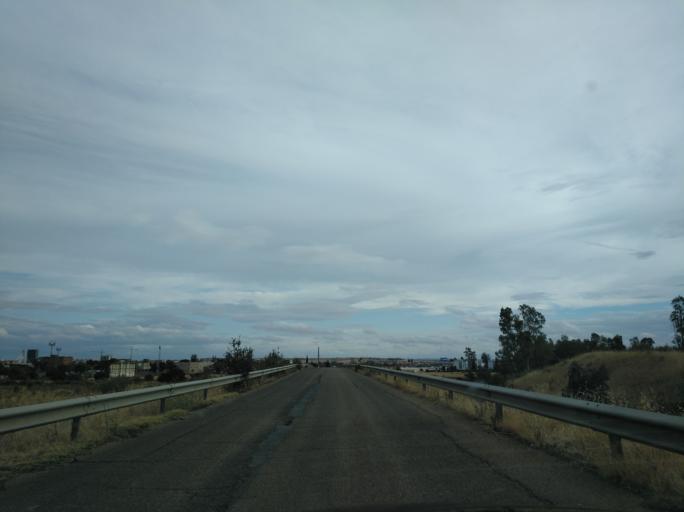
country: ES
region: Extremadura
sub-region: Provincia de Badajoz
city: Badajoz
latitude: 38.8899
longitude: -7.0164
